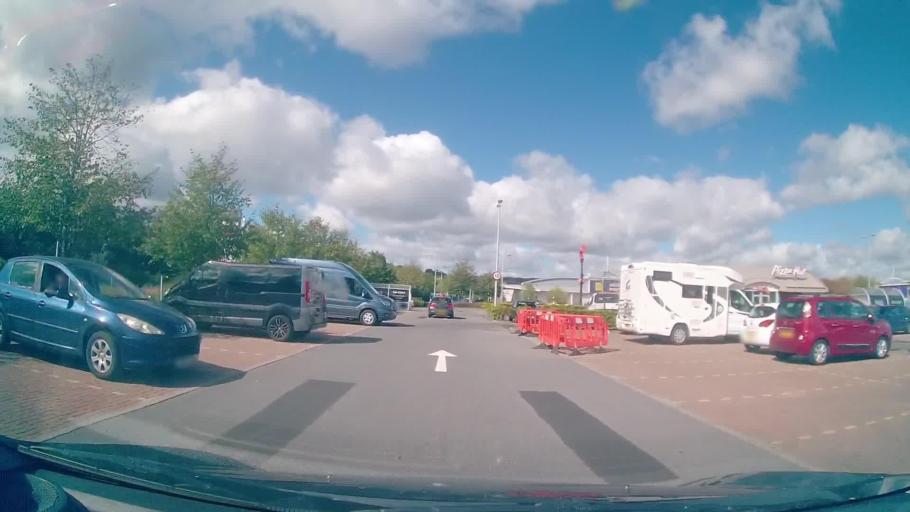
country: GB
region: Wales
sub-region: Merthyr Tydfil County Borough
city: Merthyr Tydfil
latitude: 51.7485
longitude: -3.3915
